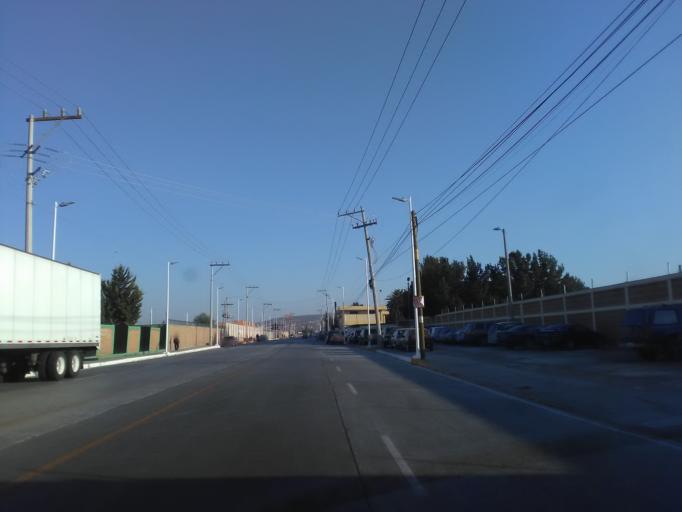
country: MX
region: Durango
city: Victoria de Durango
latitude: 24.0614
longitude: -104.6146
